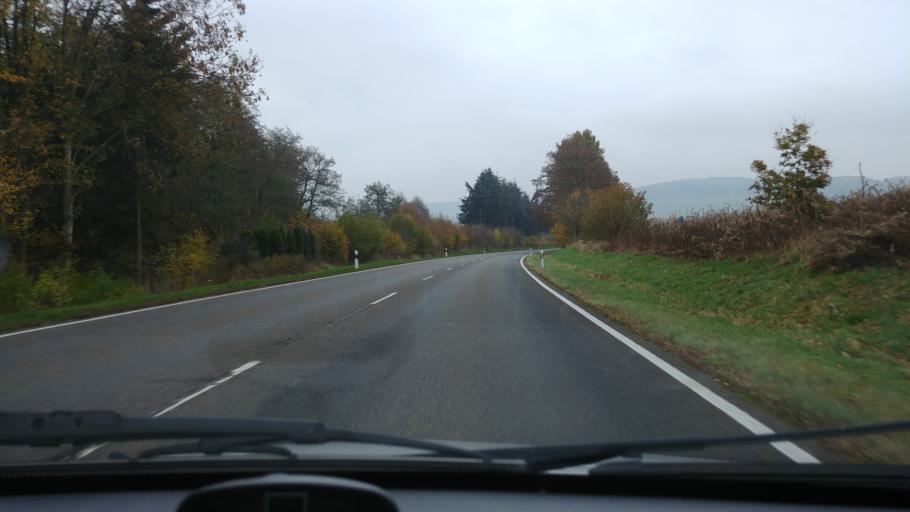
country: DE
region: Rheinland-Pfalz
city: Enspel
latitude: 50.6230
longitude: 7.8821
